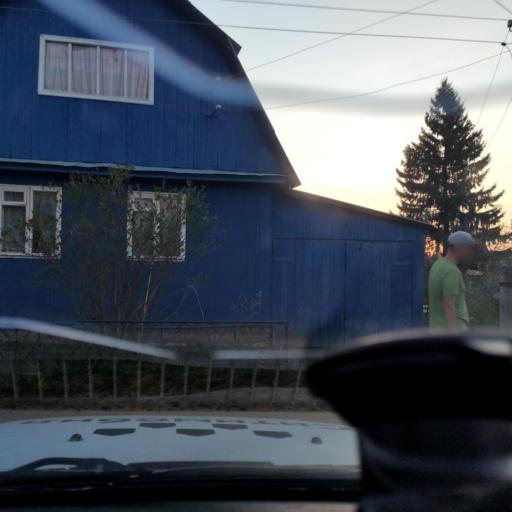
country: RU
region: Perm
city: Yug
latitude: 57.5864
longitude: 56.1997
